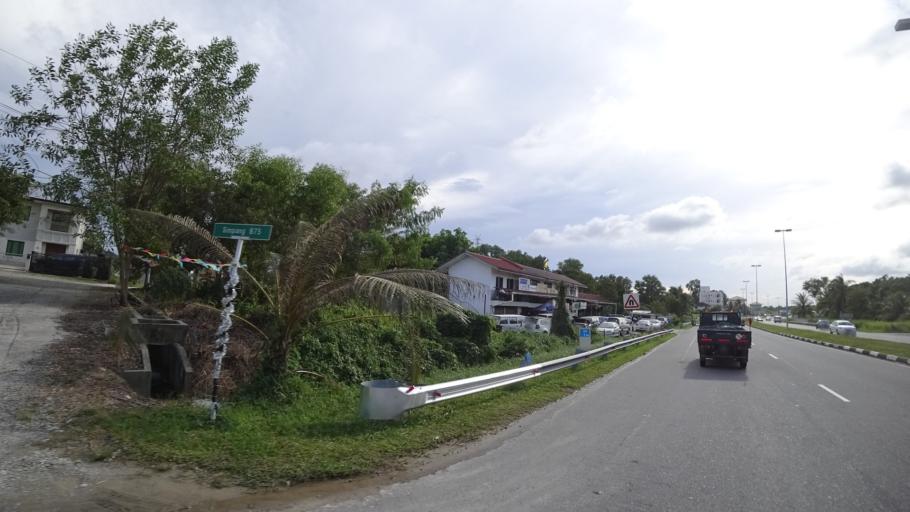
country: BN
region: Brunei and Muara
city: Bandar Seri Begawan
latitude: 4.8789
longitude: 114.8651
